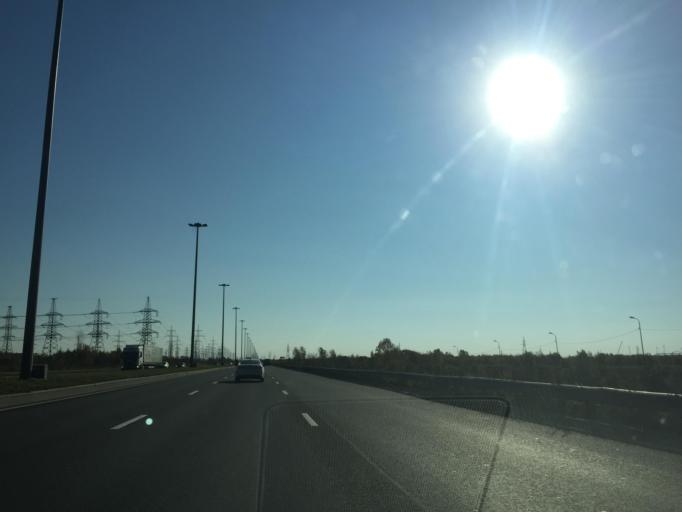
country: RU
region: St.-Petersburg
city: Petro-Slavyanka
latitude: 59.7650
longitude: 30.5044
